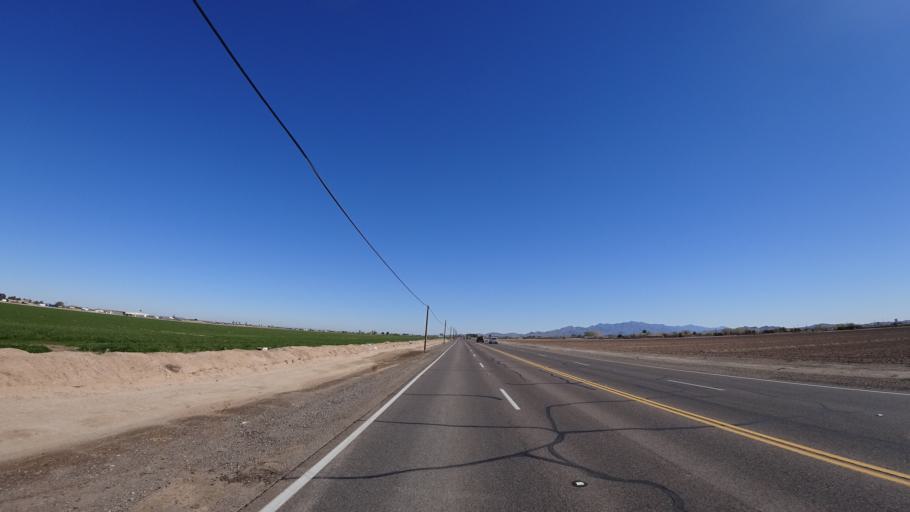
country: US
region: Arizona
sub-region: Maricopa County
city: Buckeye
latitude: 33.3776
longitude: -112.5427
